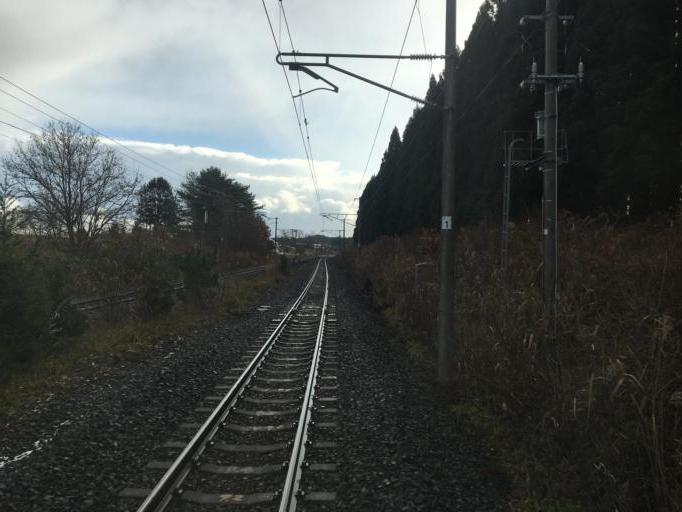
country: JP
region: Aomori
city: Aomori Shi
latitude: 40.9187
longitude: 141.0300
